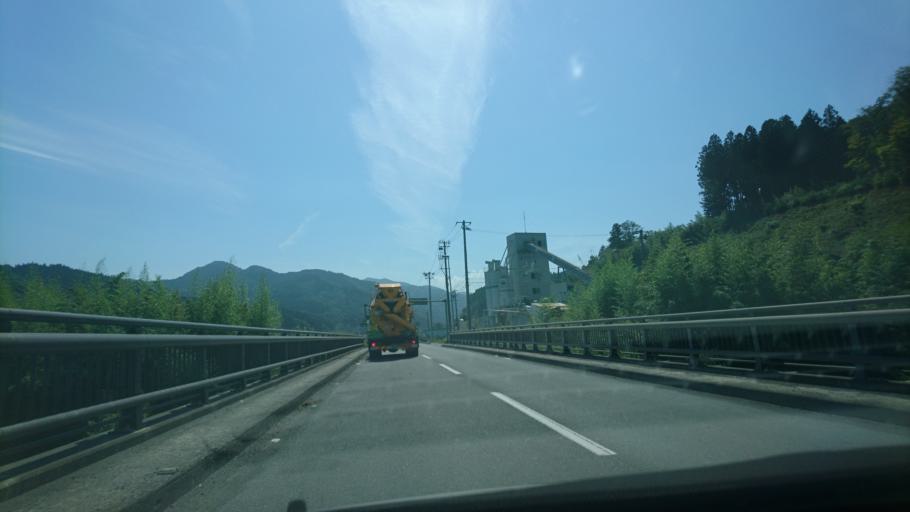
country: JP
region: Iwate
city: Ofunato
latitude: 39.0343
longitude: 141.6014
